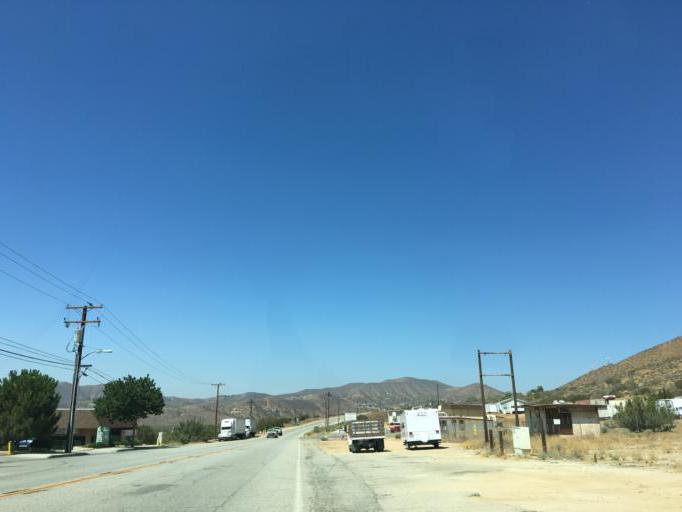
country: US
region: California
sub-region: Los Angeles County
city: Acton
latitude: 34.4928
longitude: -118.2005
